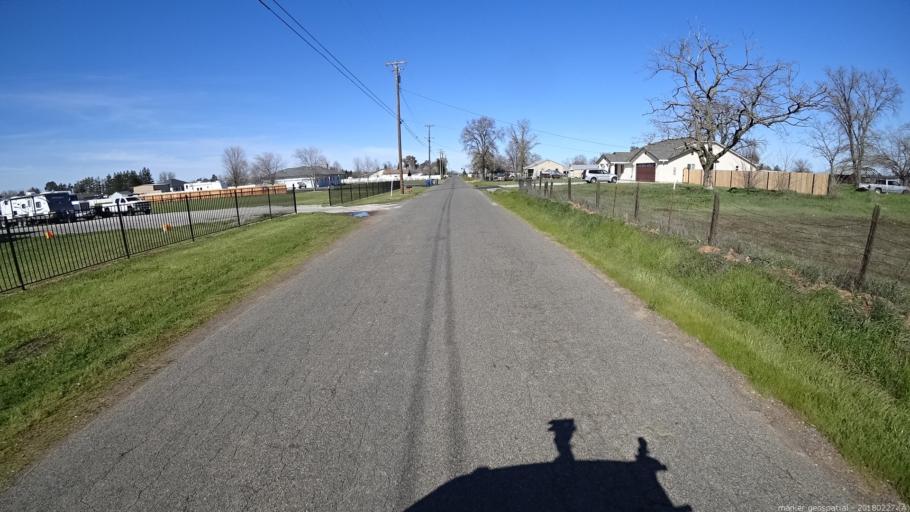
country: US
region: California
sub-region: Sacramento County
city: Elverta
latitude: 38.7103
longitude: -121.4458
